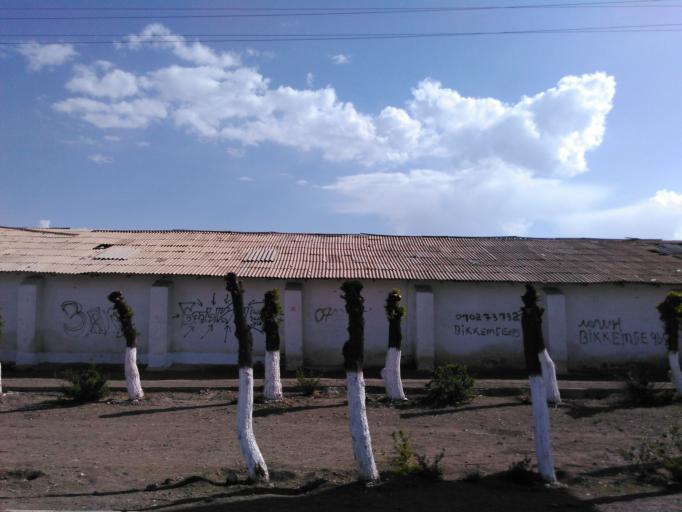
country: KG
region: Ysyk-Koel
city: Balykchy
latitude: 42.4528
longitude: 76.1643
